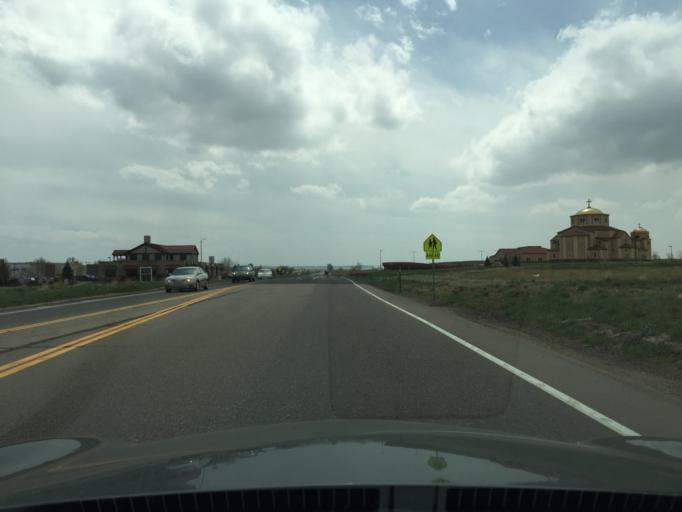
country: US
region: Colorado
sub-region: Boulder County
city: Erie
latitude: 40.0343
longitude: -105.0555
